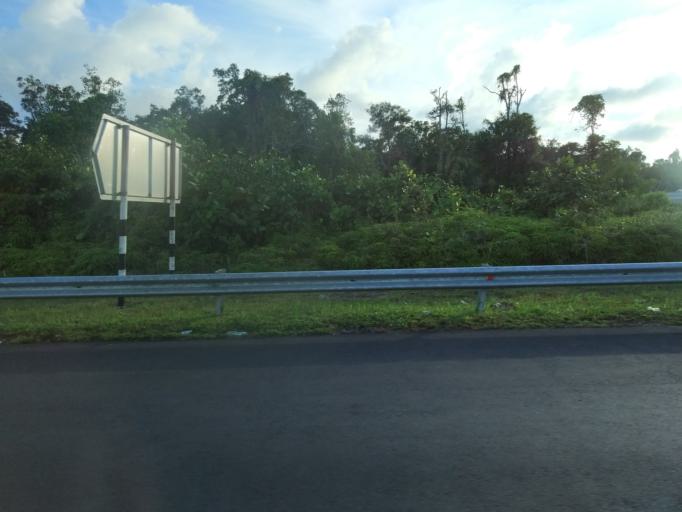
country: BN
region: Tutong
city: Tutong
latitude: 4.7778
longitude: 114.6541
